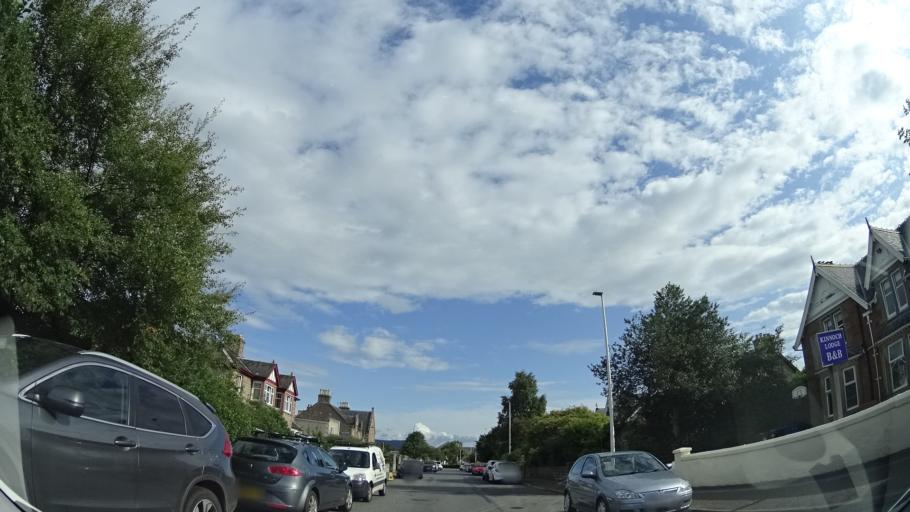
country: GB
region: Scotland
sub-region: Highland
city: Inverness
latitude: 57.4707
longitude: -4.2344
